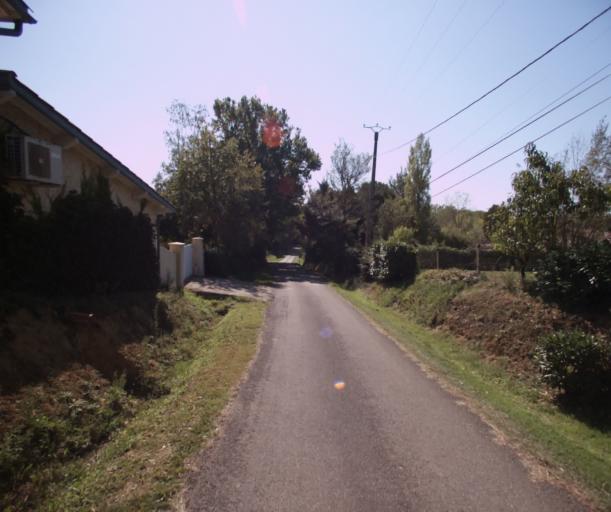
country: FR
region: Midi-Pyrenees
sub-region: Departement du Gers
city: Cazaubon
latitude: 43.9485
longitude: -0.0596
